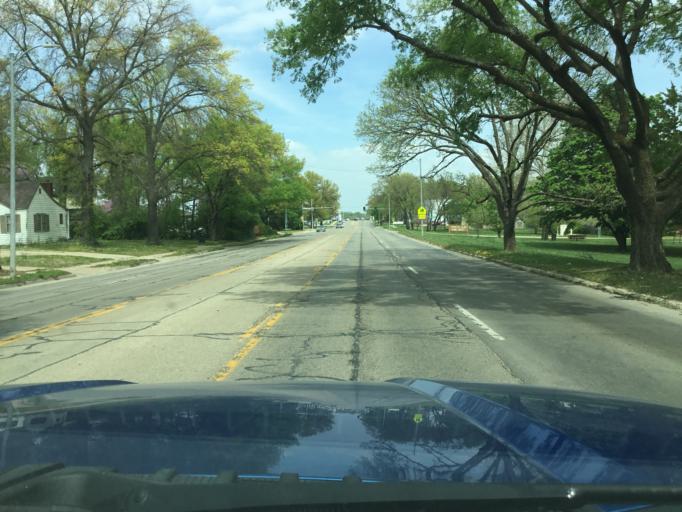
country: US
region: Kansas
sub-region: Shawnee County
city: Topeka
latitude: 39.0245
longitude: -95.6846
